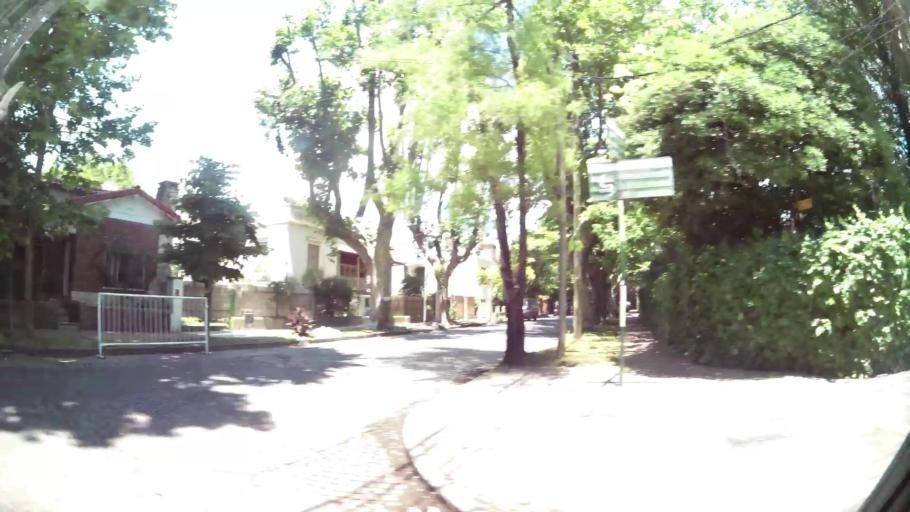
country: AR
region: Buenos Aires
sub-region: Partido de Tigre
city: Tigre
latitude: -34.4180
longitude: -58.5849
